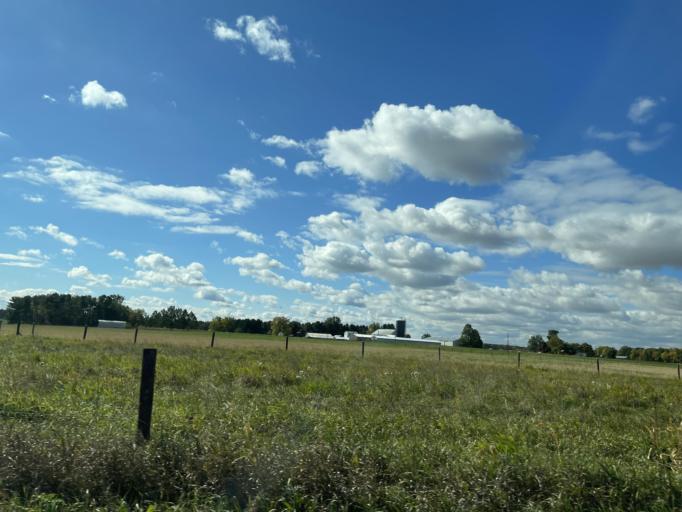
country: US
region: Indiana
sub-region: Whitley County
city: Churubusco
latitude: 41.1235
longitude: -85.2803
